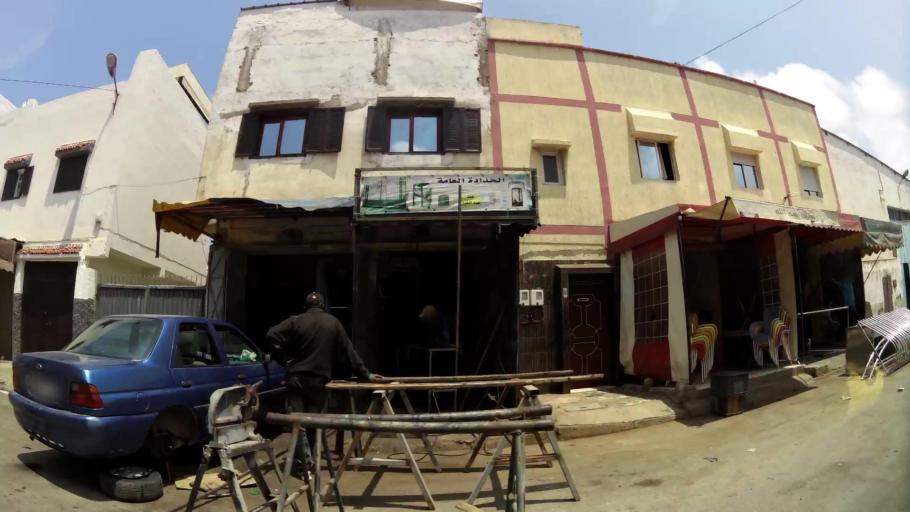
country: MA
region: Rabat-Sale-Zemmour-Zaer
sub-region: Rabat
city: Rabat
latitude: 33.9803
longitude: -6.8772
